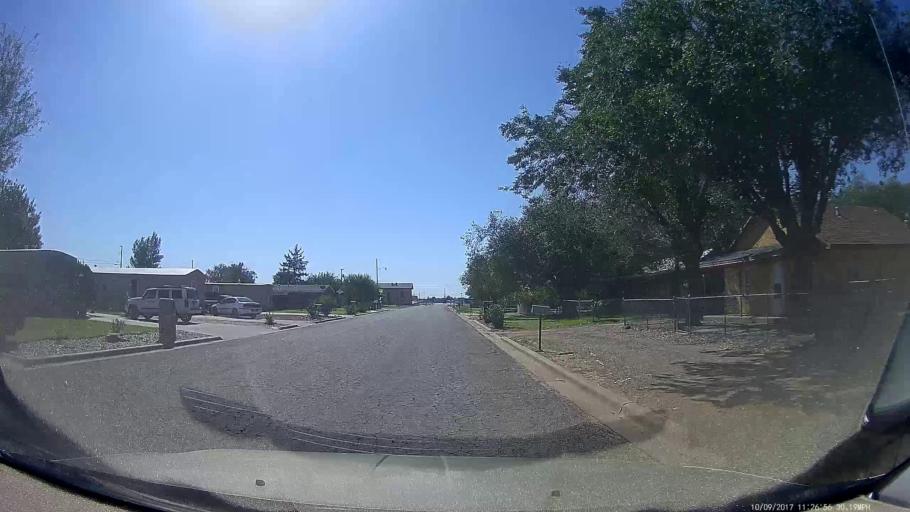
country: US
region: New Mexico
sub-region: Curry County
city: Clovis
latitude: 34.4073
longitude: -103.2272
